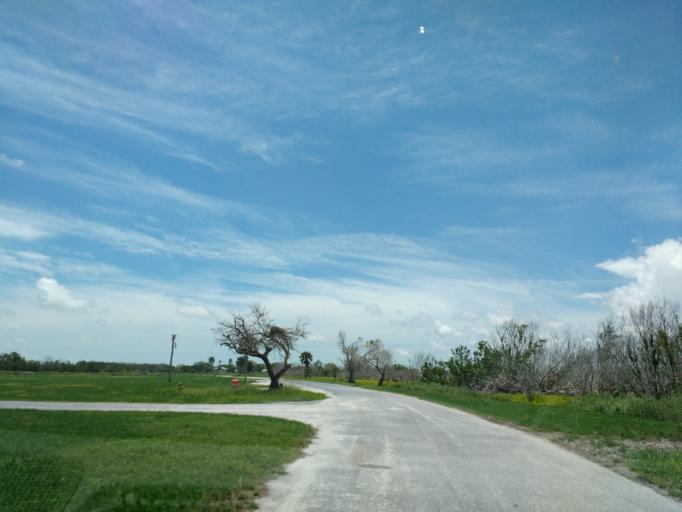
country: US
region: Florida
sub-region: Monroe County
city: Islamorada
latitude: 25.1377
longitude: -80.9334
